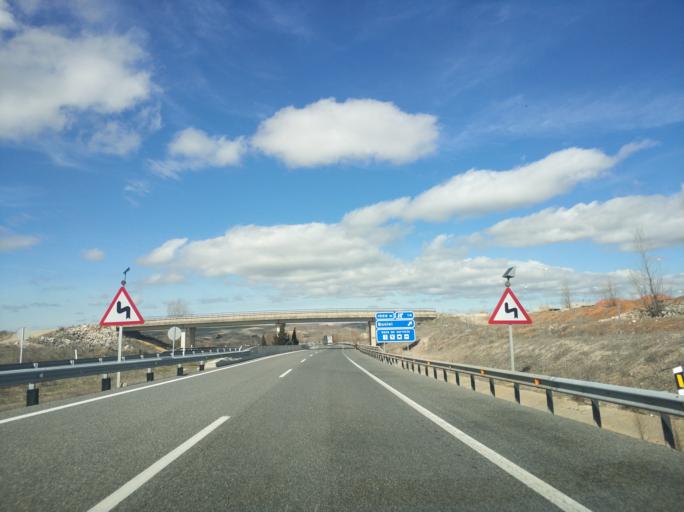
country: ES
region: Castille and Leon
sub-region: Provincia de Burgos
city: Buniel
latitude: 42.3097
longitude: -3.8115
